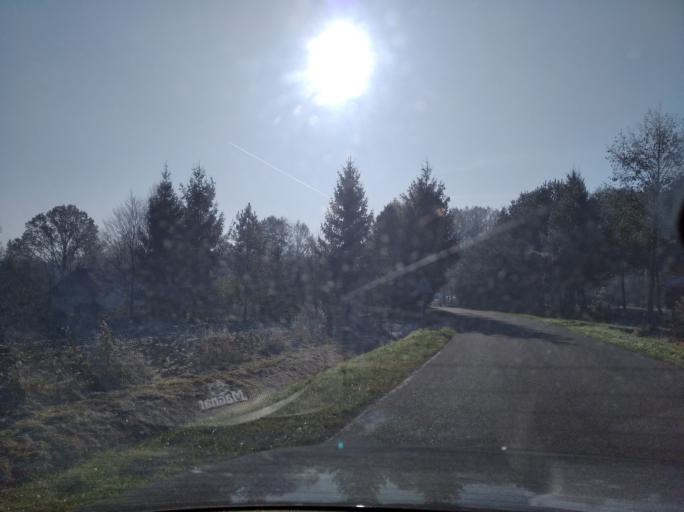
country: PL
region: Subcarpathian Voivodeship
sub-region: Powiat strzyzowski
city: Wysoka Strzyzowska
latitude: 49.8350
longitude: 21.7133
